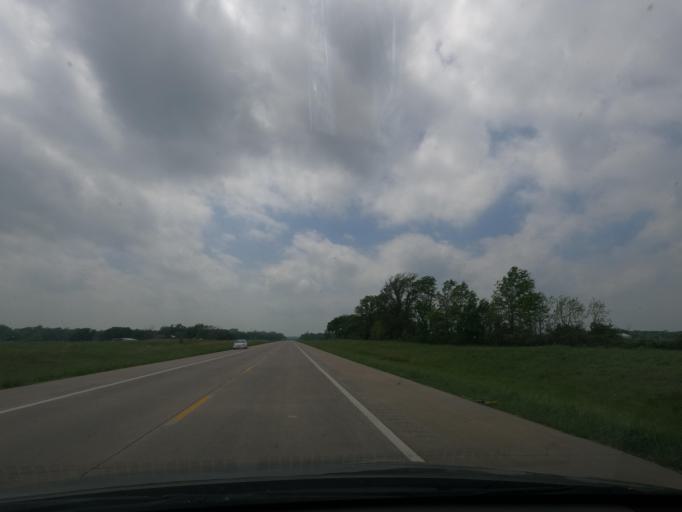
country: US
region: Kansas
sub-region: Labette County
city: Parsons
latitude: 37.3470
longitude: -95.3365
